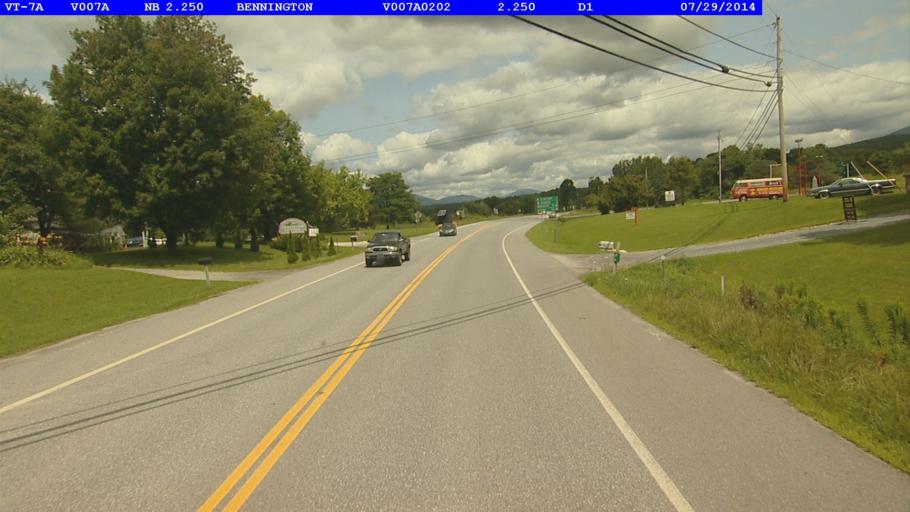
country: US
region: Vermont
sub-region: Bennington County
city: North Bennington
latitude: 42.9221
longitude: -73.2105
